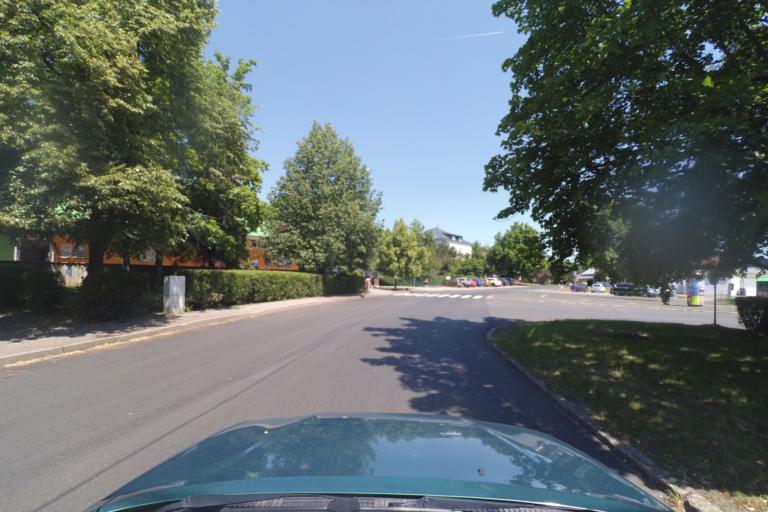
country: CZ
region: Ustecky
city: Chlumec
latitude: 50.6975
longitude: 13.9402
